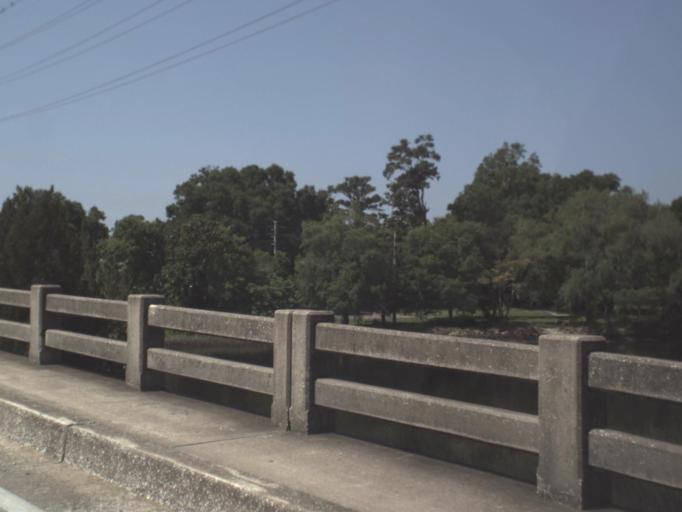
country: US
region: Florida
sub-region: Duval County
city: Jacksonville
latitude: 30.3962
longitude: -81.6831
